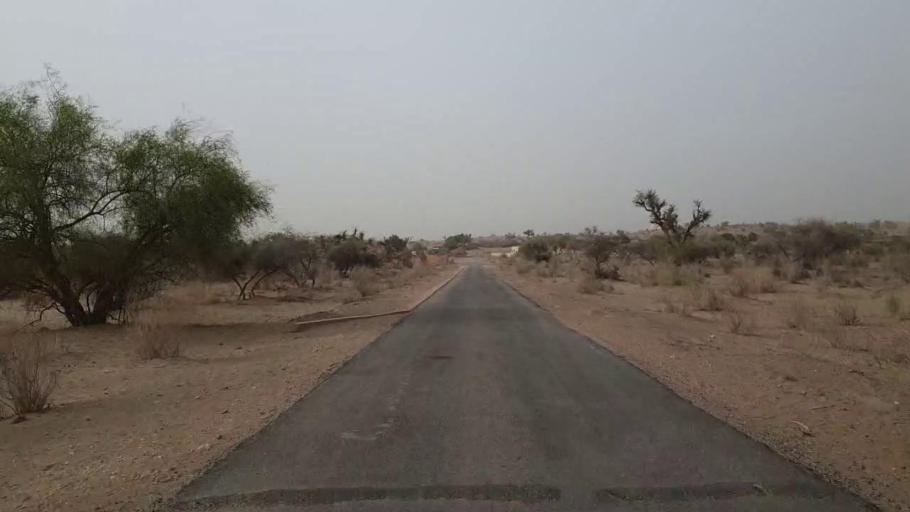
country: PK
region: Sindh
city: Islamkot
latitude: 24.5720
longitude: 70.3650
